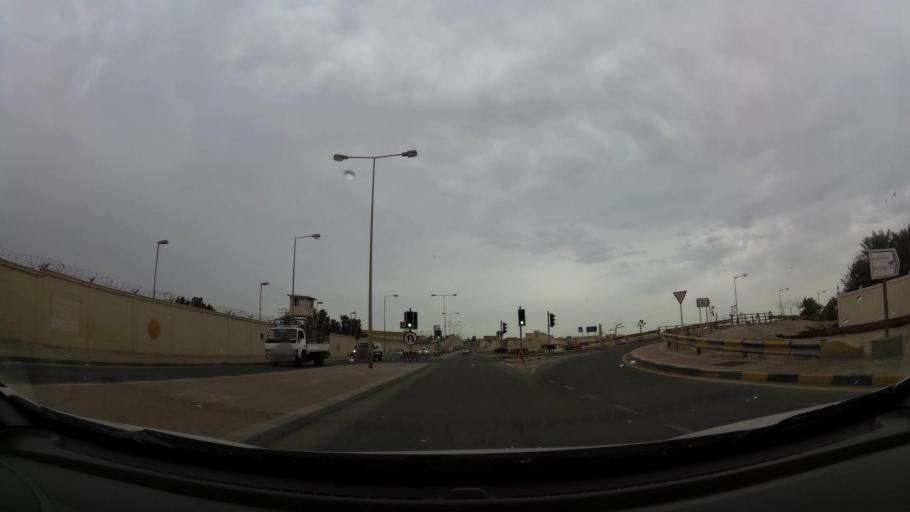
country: BH
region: Central Governorate
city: Madinat Hamad
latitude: 26.1502
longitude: 50.4862
